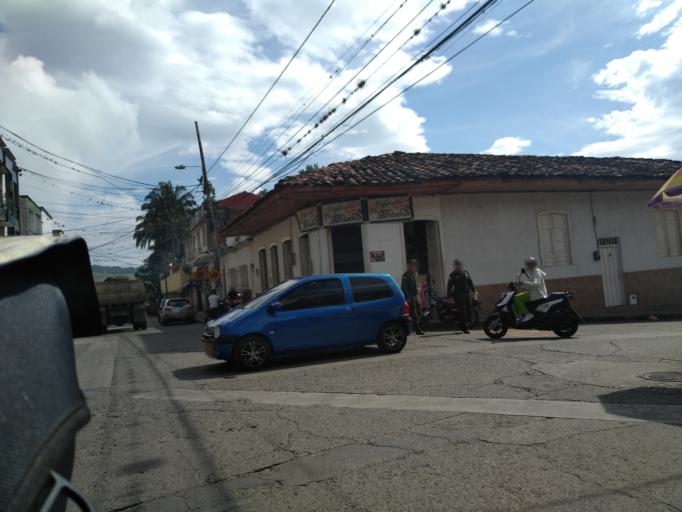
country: CO
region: Valle del Cauca
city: Caicedonia
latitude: 4.3337
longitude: -75.8290
